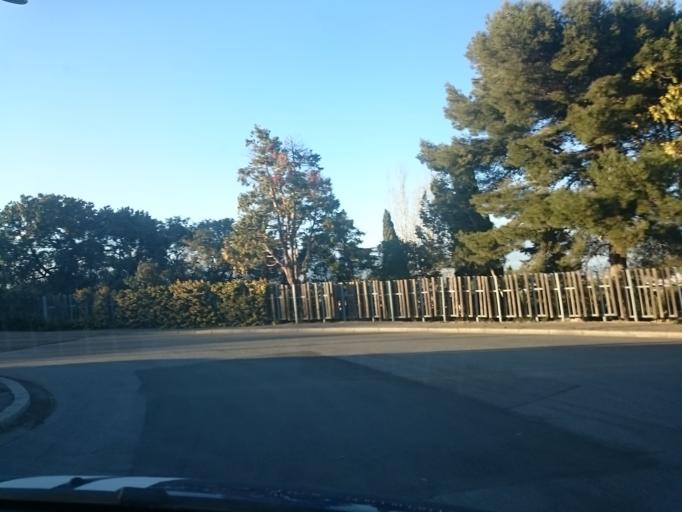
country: ES
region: Catalonia
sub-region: Provincia de Barcelona
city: Sants-Montjuic
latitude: 41.3671
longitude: 2.1636
